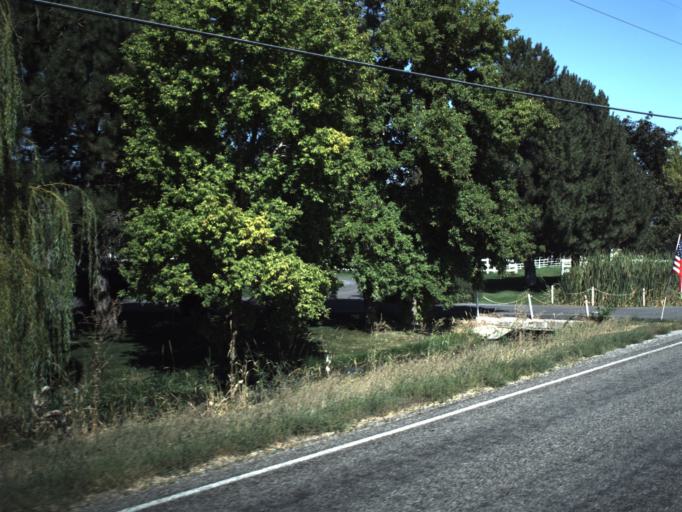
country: US
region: Utah
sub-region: Cache County
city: Hyrum
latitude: 41.5841
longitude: -111.8383
